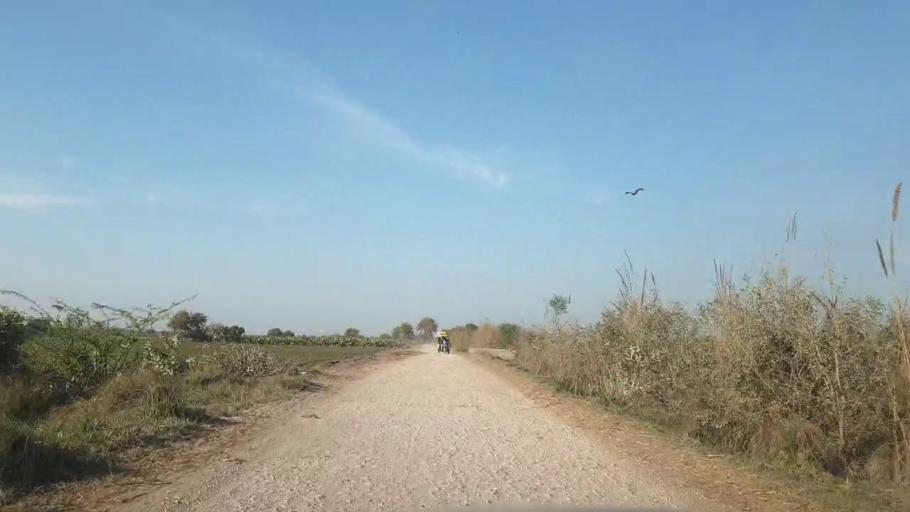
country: PK
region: Sindh
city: Tando Adam
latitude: 25.7136
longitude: 68.7039
